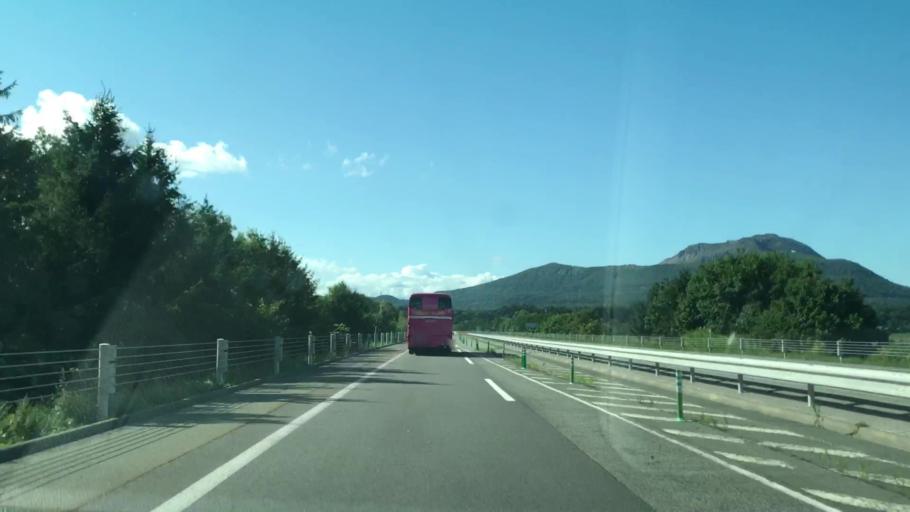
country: JP
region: Hokkaido
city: Date
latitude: 42.4906
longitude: 140.8799
